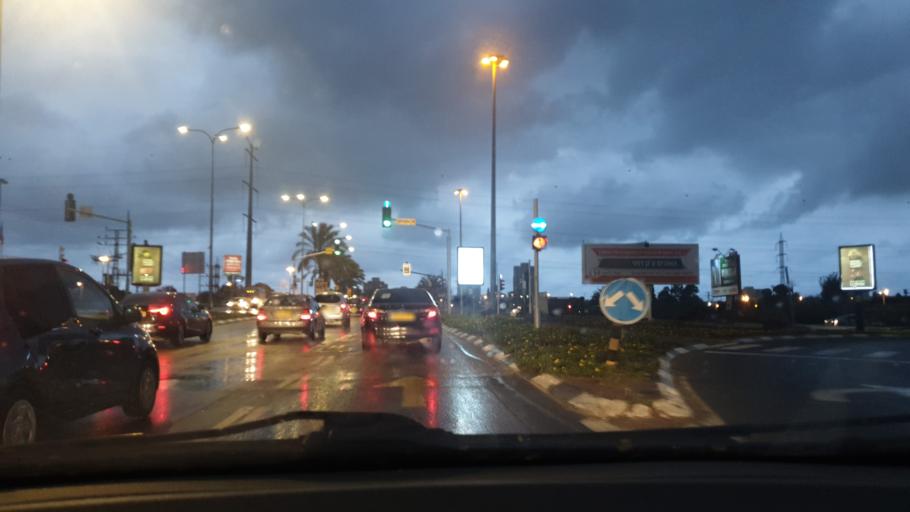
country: IL
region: Central District
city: Rishon LeZiyyon
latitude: 31.9769
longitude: 34.7946
